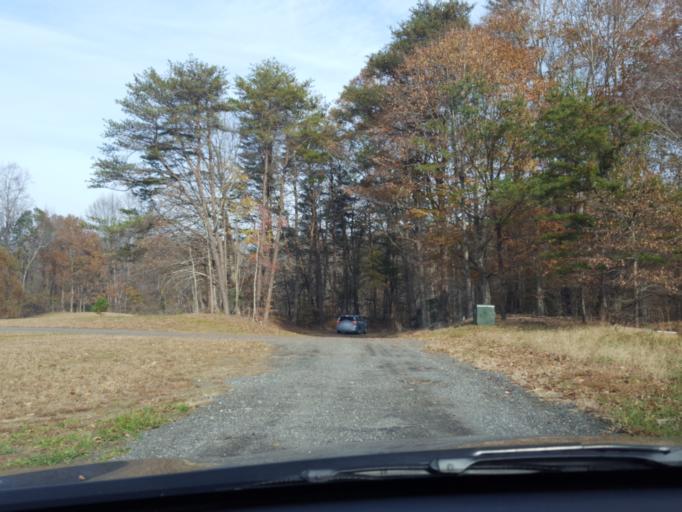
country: US
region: Maryland
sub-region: Calvert County
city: Prince Frederick
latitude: 38.5455
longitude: -76.5571
